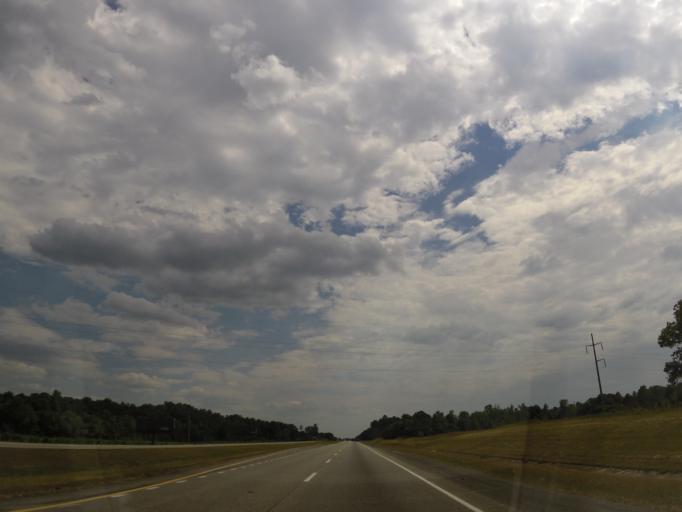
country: US
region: Alabama
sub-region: Jackson County
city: Bridgeport
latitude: 34.9620
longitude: -85.7447
